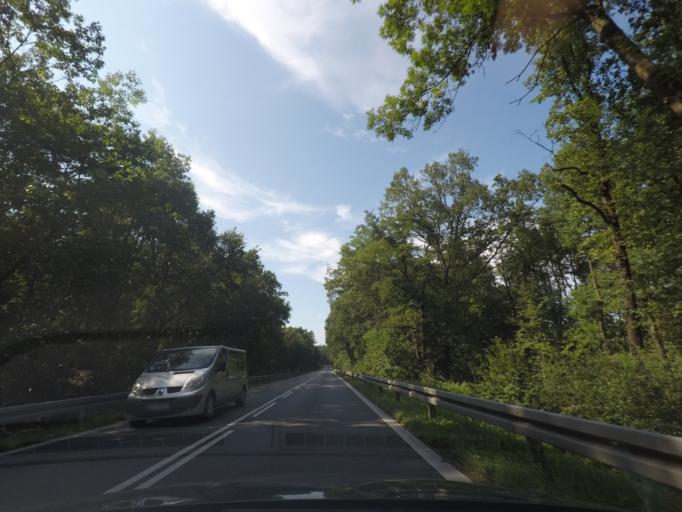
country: PL
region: Silesian Voivodeship
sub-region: Powiat pszczynski
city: Radostowice
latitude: 50.0167
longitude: 18.8500
